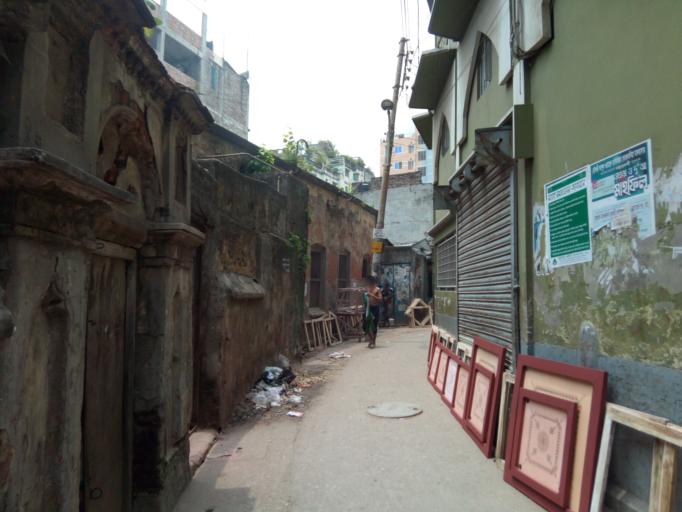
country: BD
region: Dhaka
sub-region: Dhaka
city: Dhaka
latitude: 23.7200
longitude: 90.4038
